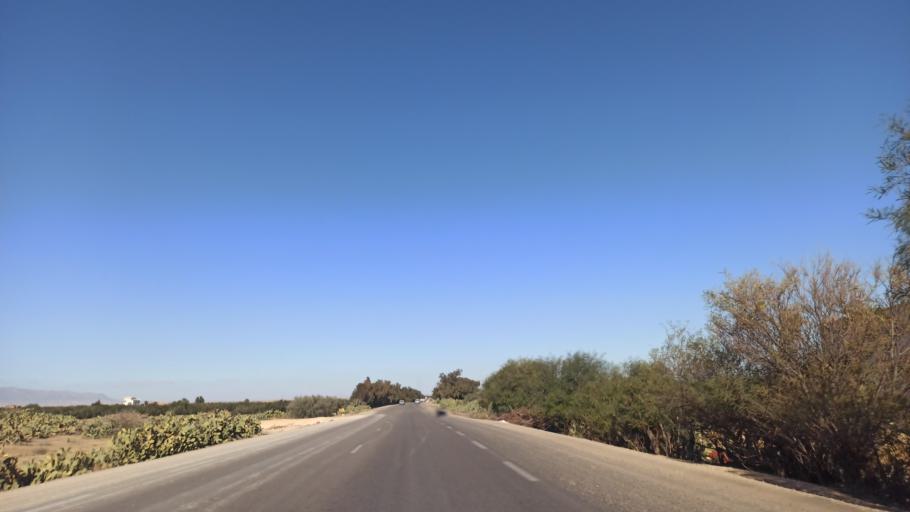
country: TN
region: Sidi Bu Zayd
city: Jilma
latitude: 35.1516
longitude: 9.3644
